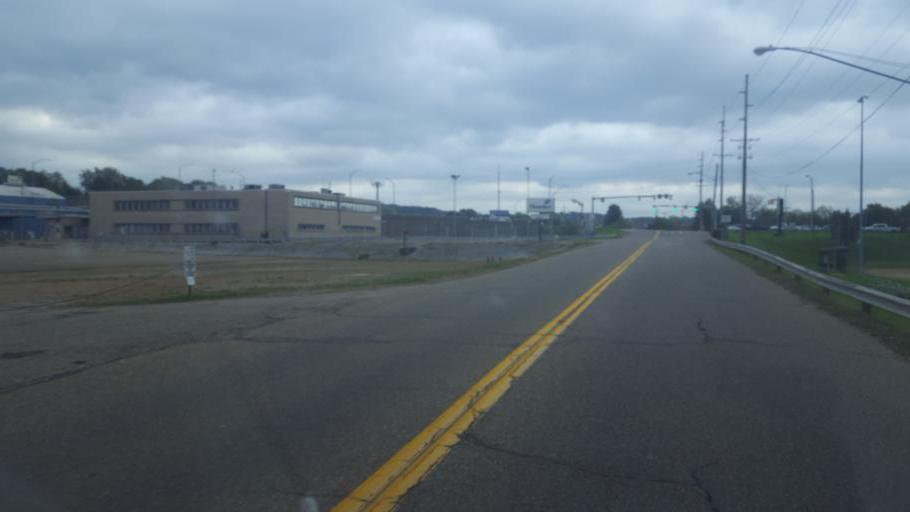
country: US
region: Ohio
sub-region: Tuscarawas County
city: New Philadelphia
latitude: 40.4838
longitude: -81.4489
